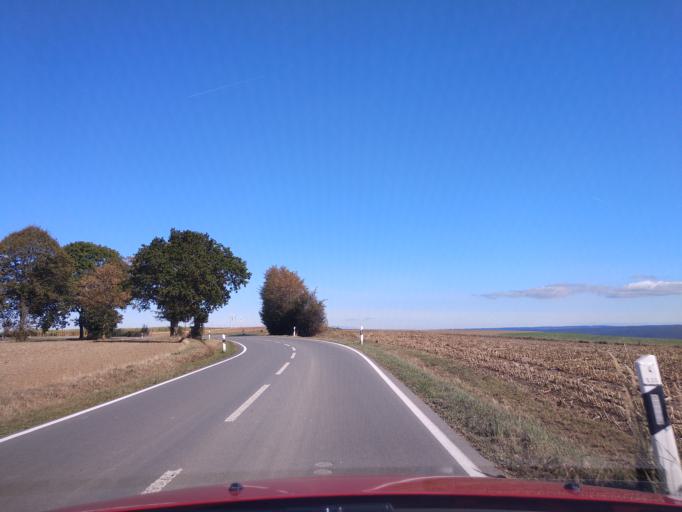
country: DE
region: Lower Saxony
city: Boffzen
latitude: 51.7420
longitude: 9.3030
